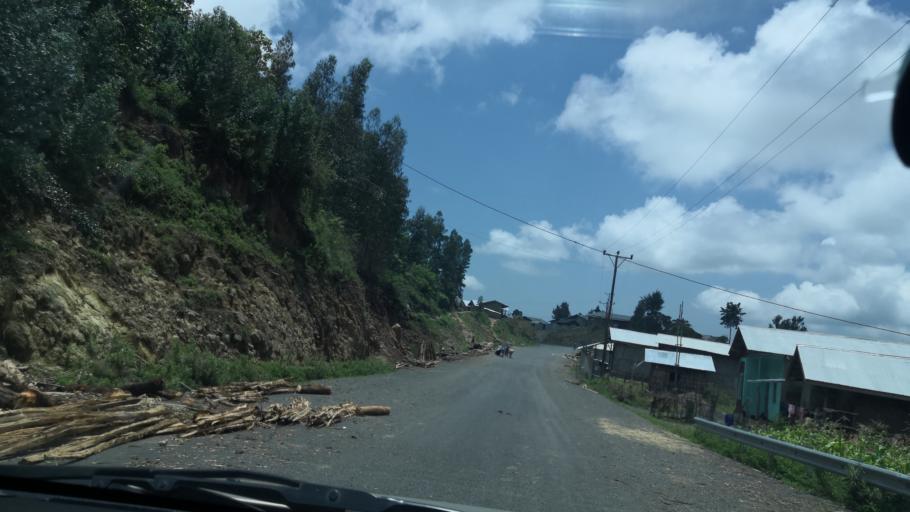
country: ET
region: Amhara
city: Abomsa
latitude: 10.3225
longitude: 39.8507
